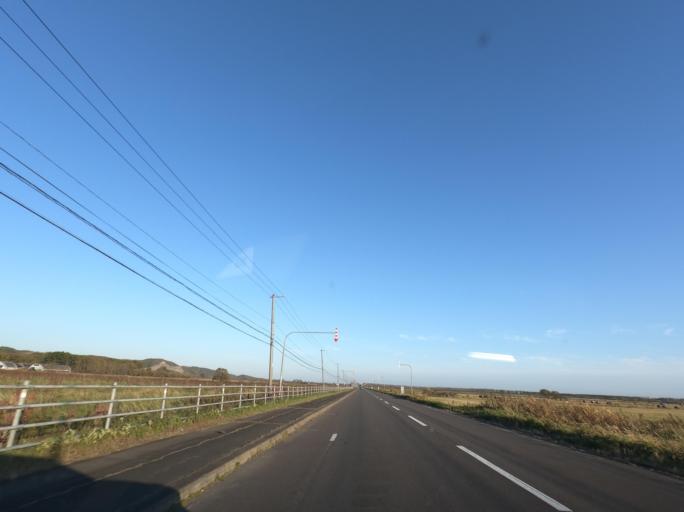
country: JP
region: Hokkaido
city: Kushiro
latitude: 43.0702
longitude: 144.2572
